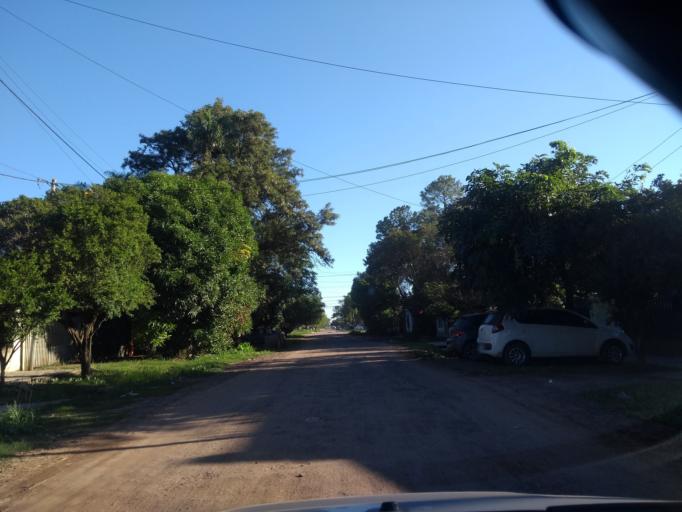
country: AR
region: Chaco
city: Barranqueras
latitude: -27.4849
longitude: -58.9471
